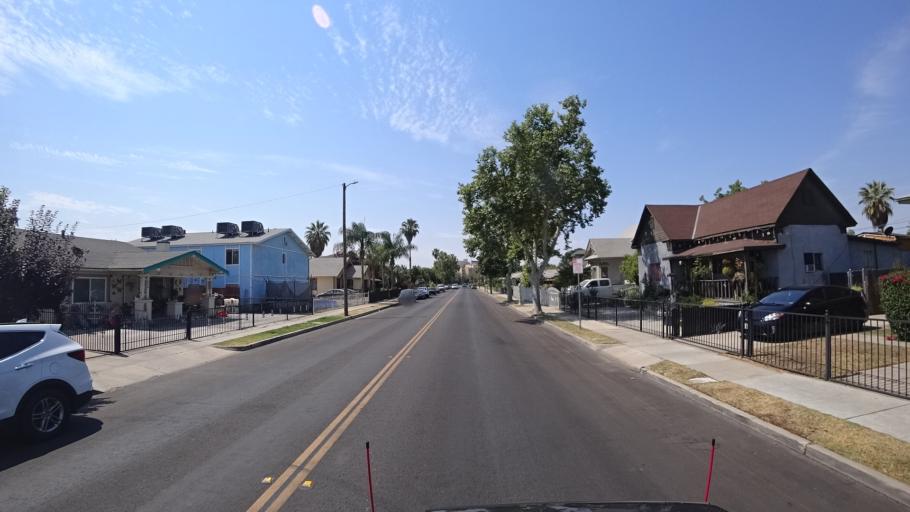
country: US
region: California
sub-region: Fresno County
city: Fresno
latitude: 36.7465
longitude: -119.7947
